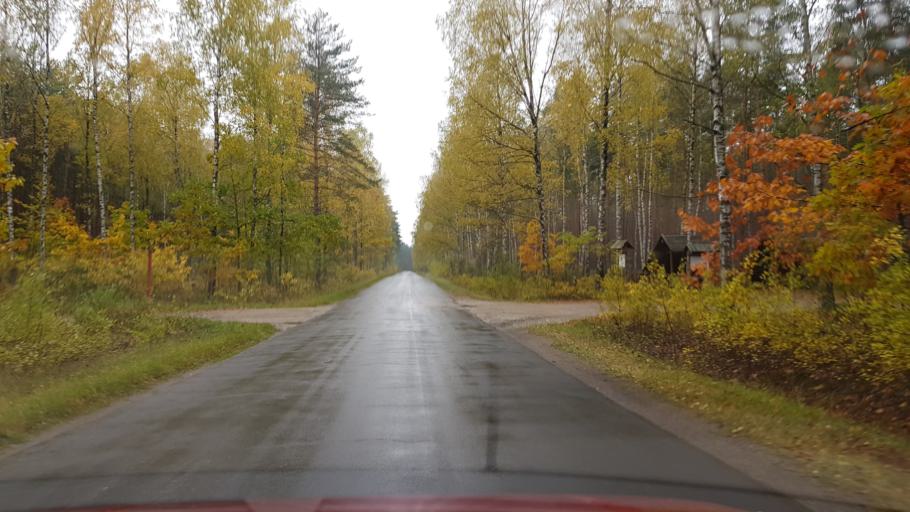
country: PL
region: West Pomeranian Voivodeship
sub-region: Powiat walecki
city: Walcz
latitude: 53.3719
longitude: 16.4445
